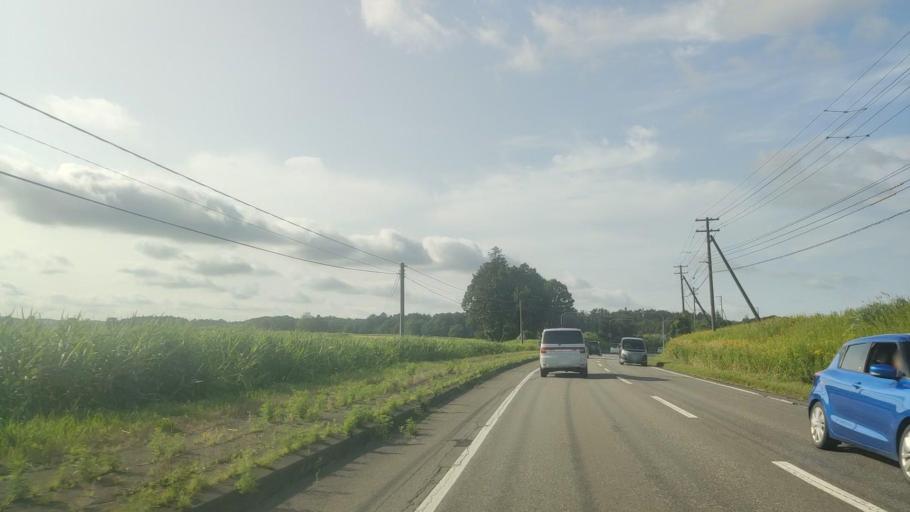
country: JP
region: Hokkaido
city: Chitose
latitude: 42.8018
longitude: 141.8347
